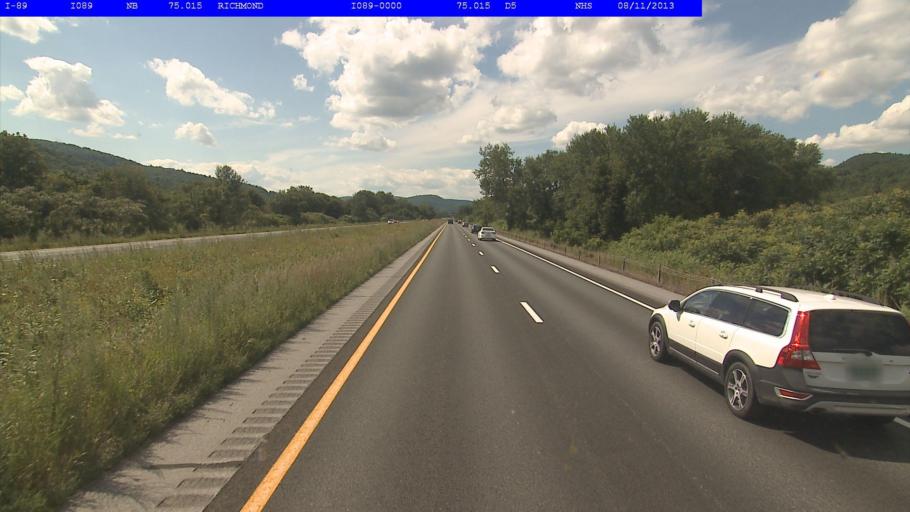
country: US
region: Vermont
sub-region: Chittenden County
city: Williston
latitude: 44.3936
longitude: -72.9621
